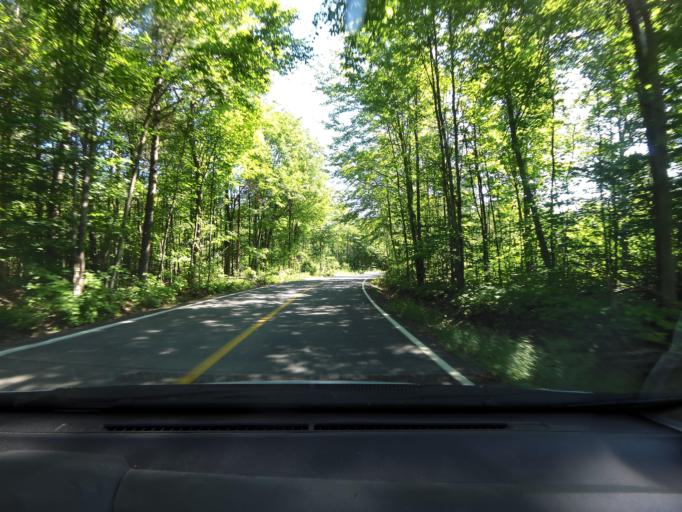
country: CA
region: Quebec
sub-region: Mauricie
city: Becancour
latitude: 46.5523
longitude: -72.4210
